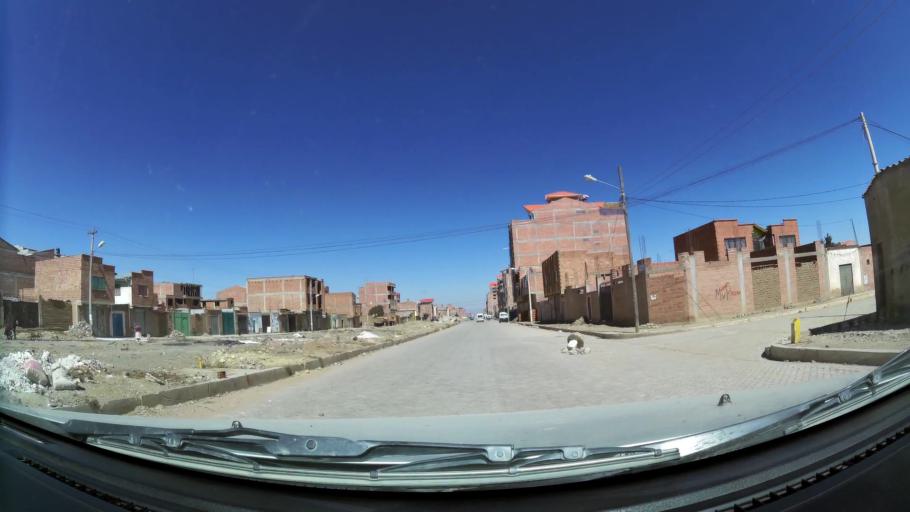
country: BO
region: La Paz
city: La Paz
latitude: -16.5384
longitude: -68.1955
